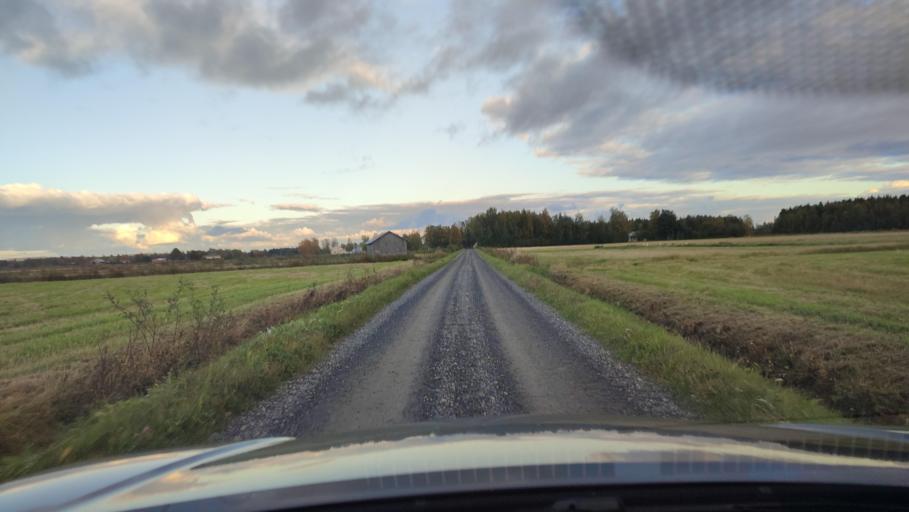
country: FI
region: Ostrobothnia
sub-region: Sydosterbotten
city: Kristinestad
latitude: 62.2501
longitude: 21.4717
